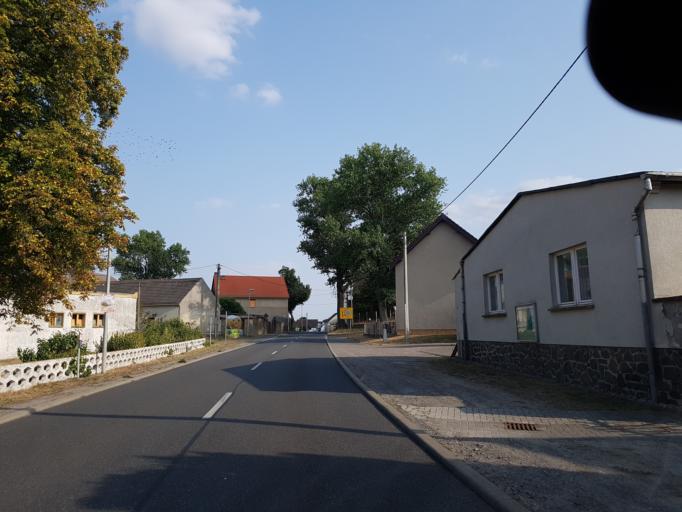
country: DE
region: Saxony
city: Dommitzsch
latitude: 51.6627
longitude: 12.8519
